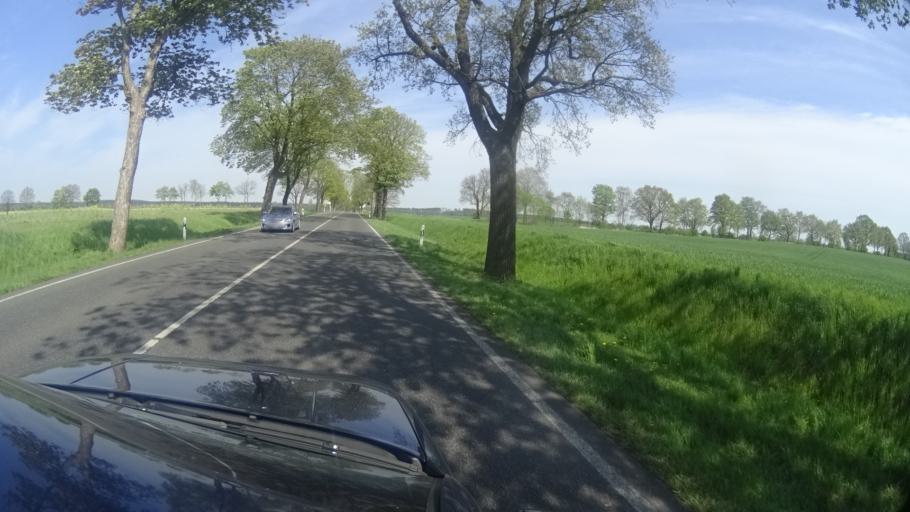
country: DE
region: Brandenburg
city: Pessin
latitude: 52.6814
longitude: 12.6171
